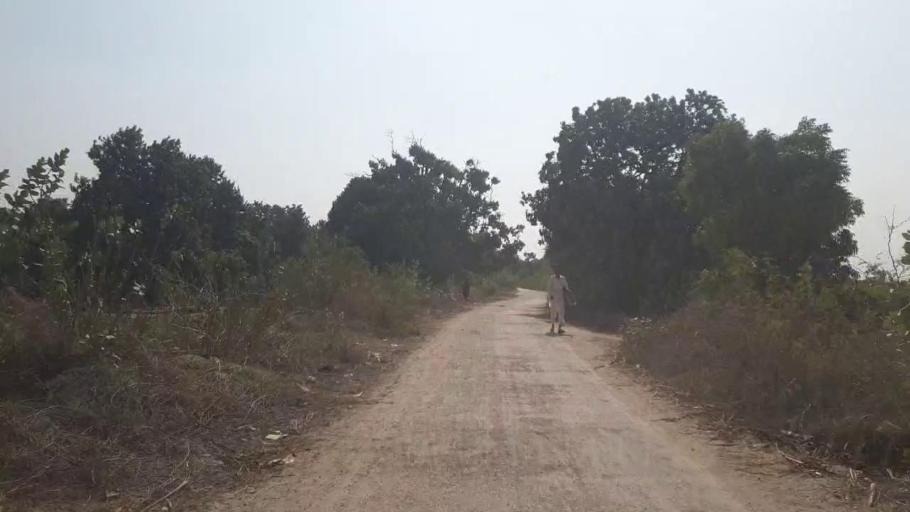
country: PK
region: Sindh
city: Tando Allahyar
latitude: 25.4862
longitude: 68.8481
